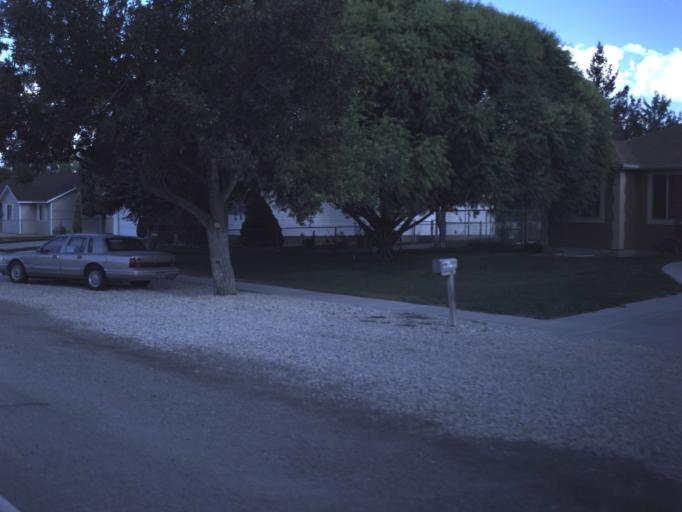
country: US
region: Utah
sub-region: Tooele County
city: Grantsville
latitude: 40.5999
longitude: -112.4748
